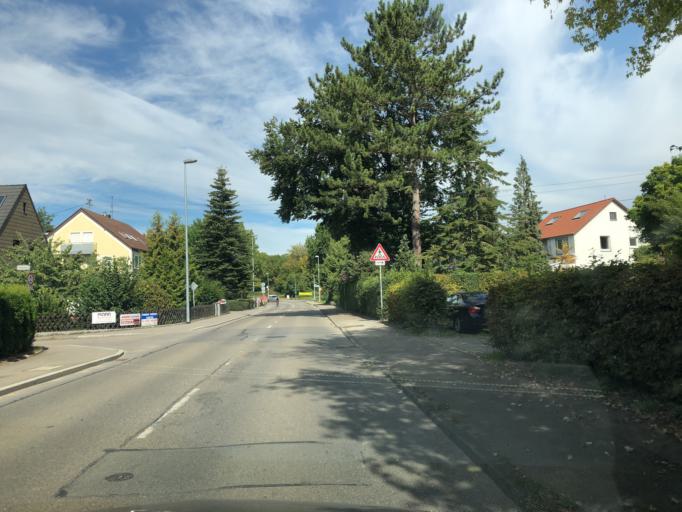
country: DE
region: Baden-Wuerttemberg
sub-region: Regierungsbezirk Stuttgart
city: Nurtingen
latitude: 48.6389
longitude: 9.3519
